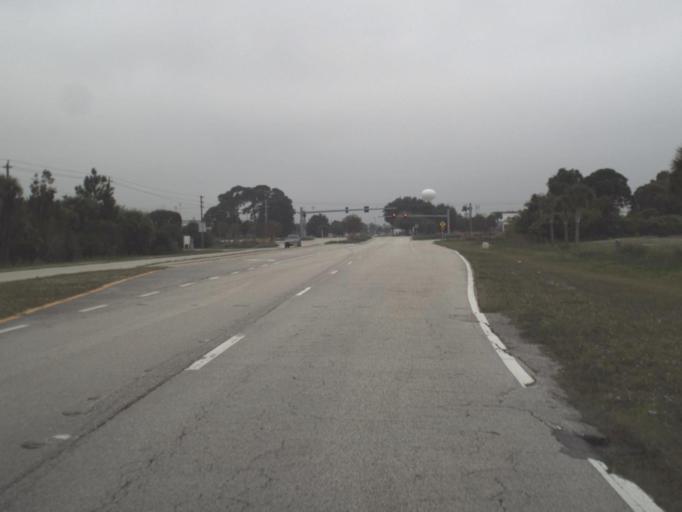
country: US
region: Florida
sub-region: Brevard County
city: Palm Bay
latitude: 28.0369
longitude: -80.5974
